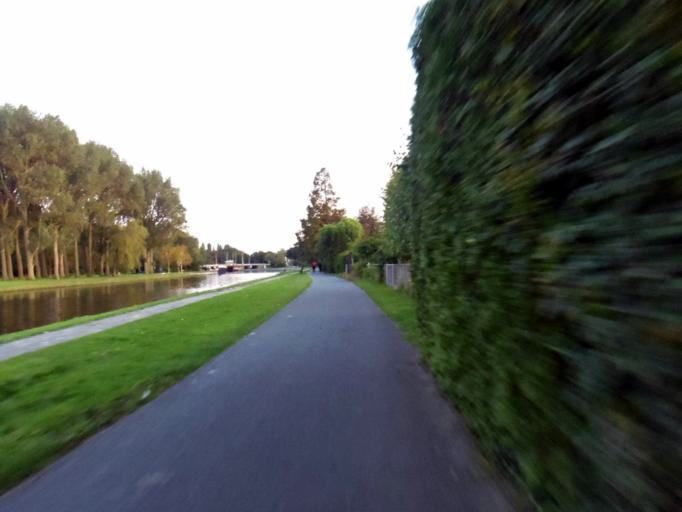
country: NL
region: South Holland
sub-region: Gemeente Voorschoten
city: Voorschoten
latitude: 52.1393
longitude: 4.4665
